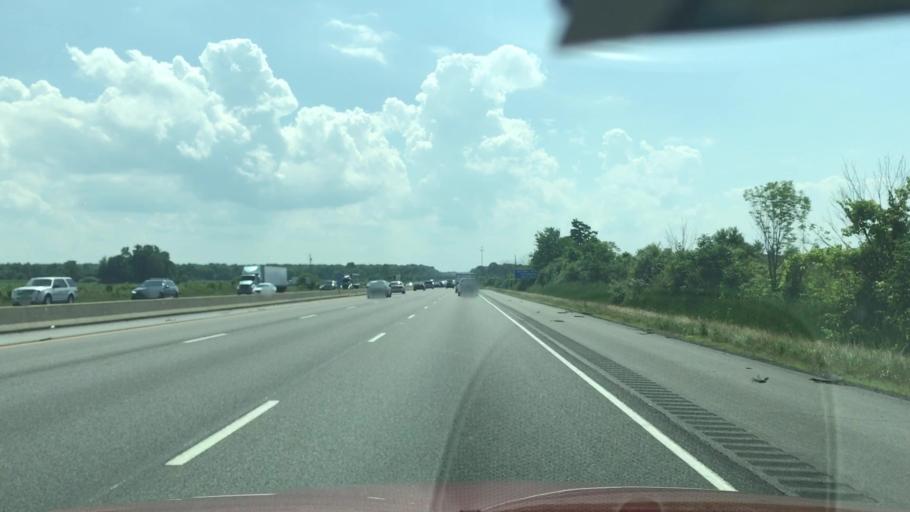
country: US
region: Michigan
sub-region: Berrien County
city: New Buffalo
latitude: 41.7439
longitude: -86.7770
